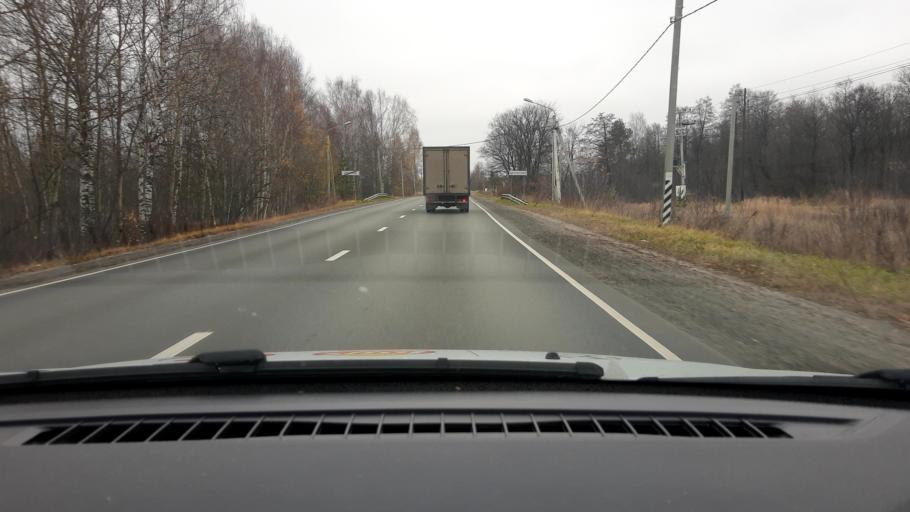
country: RU
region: Nizjnij Novgorod
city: Gorodets
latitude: 56.6027
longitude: 43.4500
